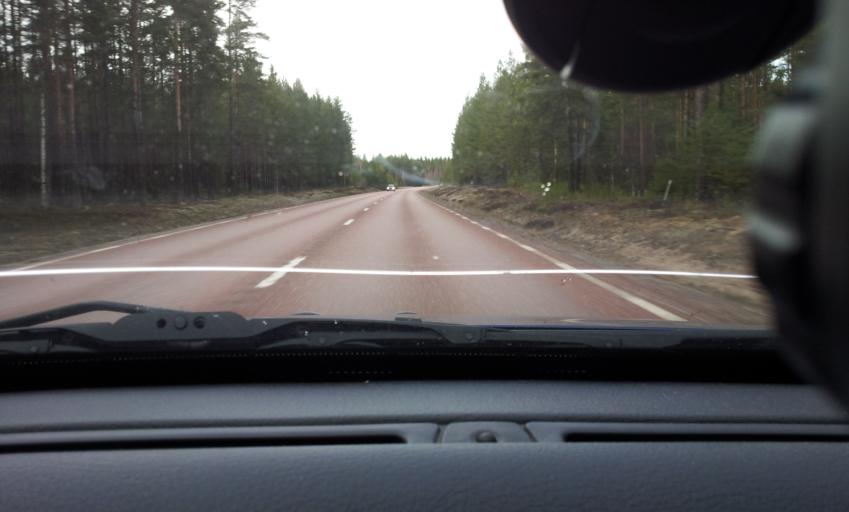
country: SE
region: Gaevleborg
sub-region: Ljusdals Kommun
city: Farila
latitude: 61.8288
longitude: 15.7531
